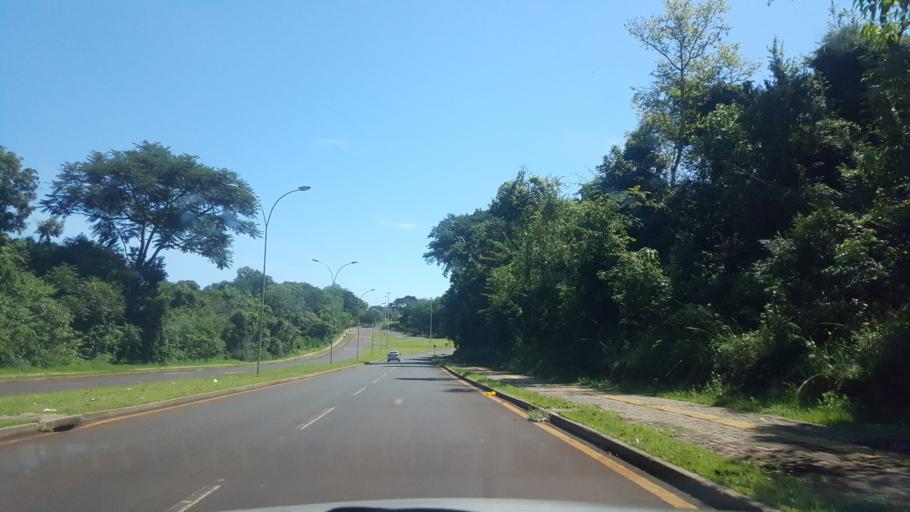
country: AR
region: Misiones
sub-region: Departamento de Iguazu
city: Puerto Iguazu
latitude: -25.5704
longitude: -54.5591
